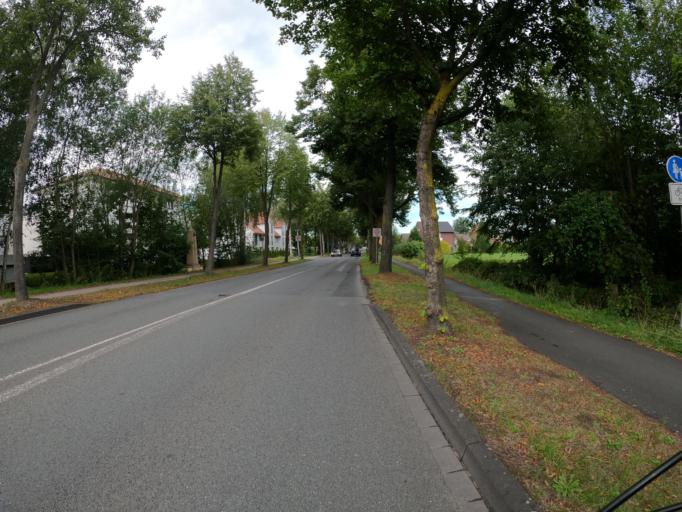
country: DE
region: North Rhine-Westphalia
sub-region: Regierungsbezirk Arnsberg
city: Lippstadt
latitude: 51.7054
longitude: 8.3386
